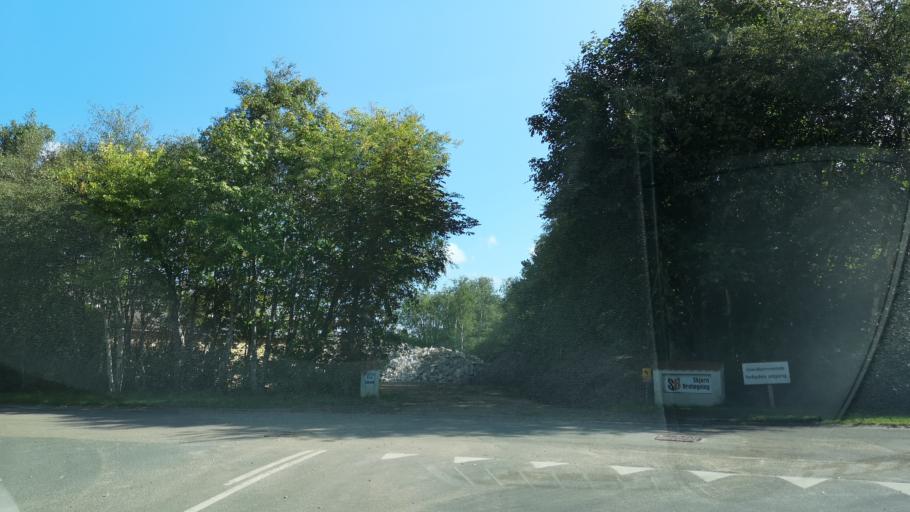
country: DK
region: Central Jutland
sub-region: Ringkobing-Skjern Kommune
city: Skjern
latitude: 55.9554
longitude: 8.4951
